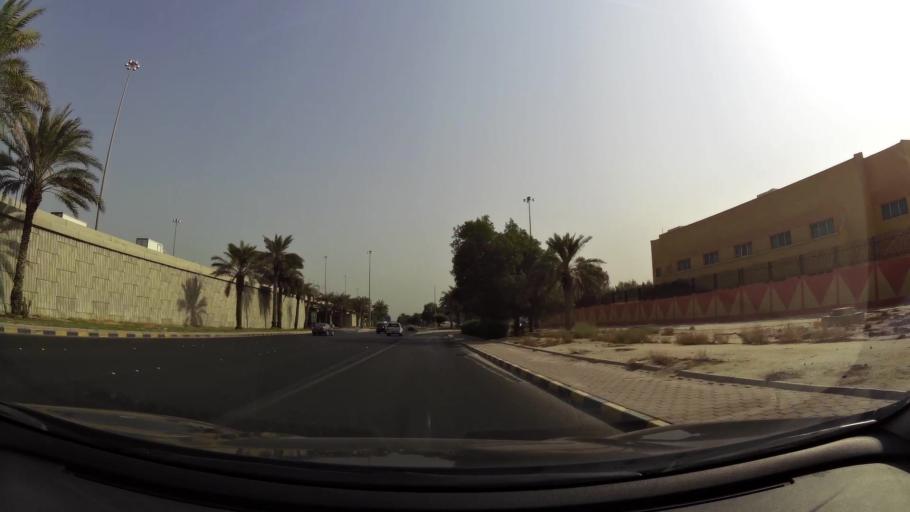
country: KW
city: Bayan
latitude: 29.3049
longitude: 48.0599
